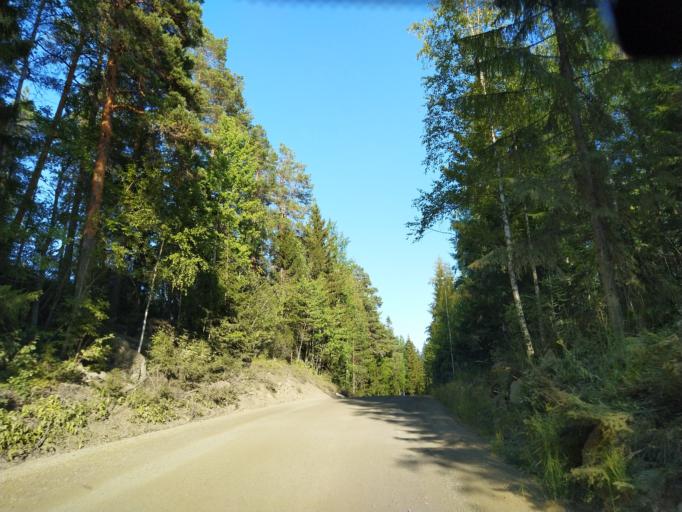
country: FI
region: Central Finland
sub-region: Jaemsae
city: Kuhmoinen
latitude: 61.6109
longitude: 25.1203
